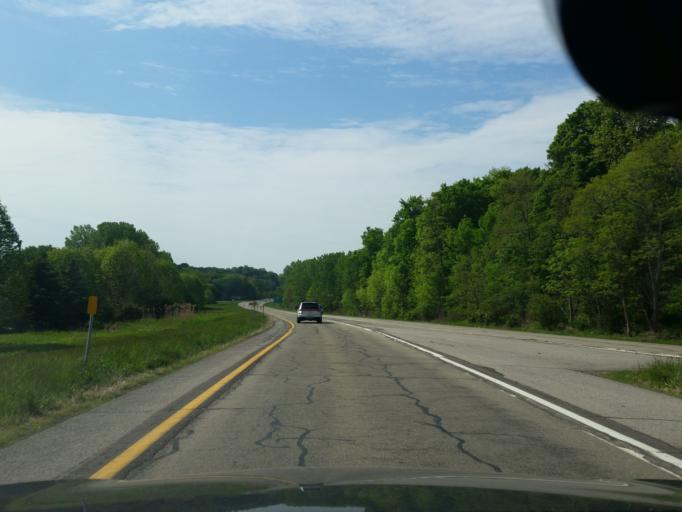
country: US
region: New York
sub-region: Chautauqua County
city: Lakewood
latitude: 42.1568
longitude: -79.3748
